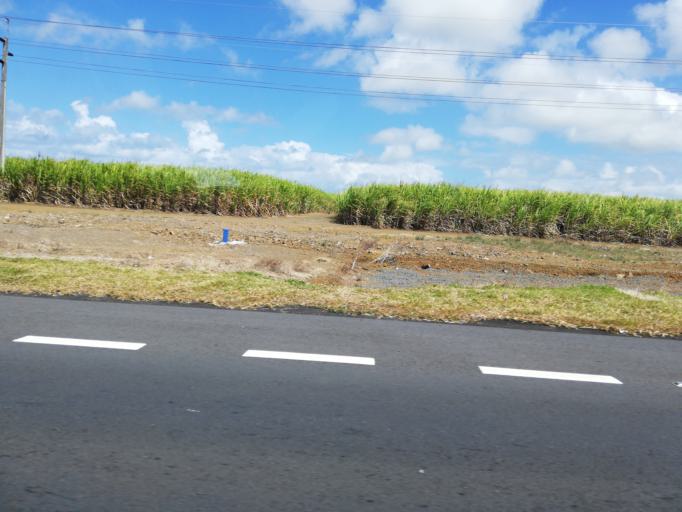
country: MU
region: Grand Port
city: Plaine Magnien
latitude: -20.4377
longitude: 57.6527
